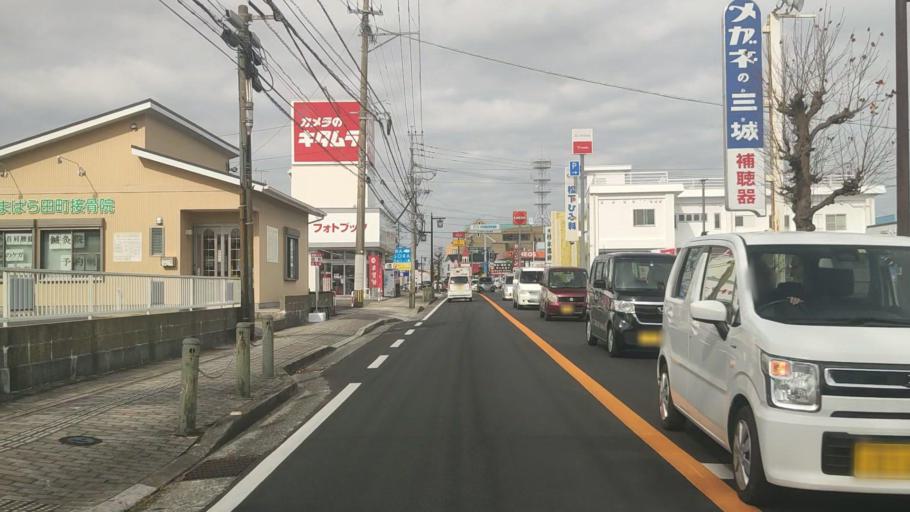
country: JP
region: Nagasaki
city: Shimabara
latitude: 32.7954
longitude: 130.3679
